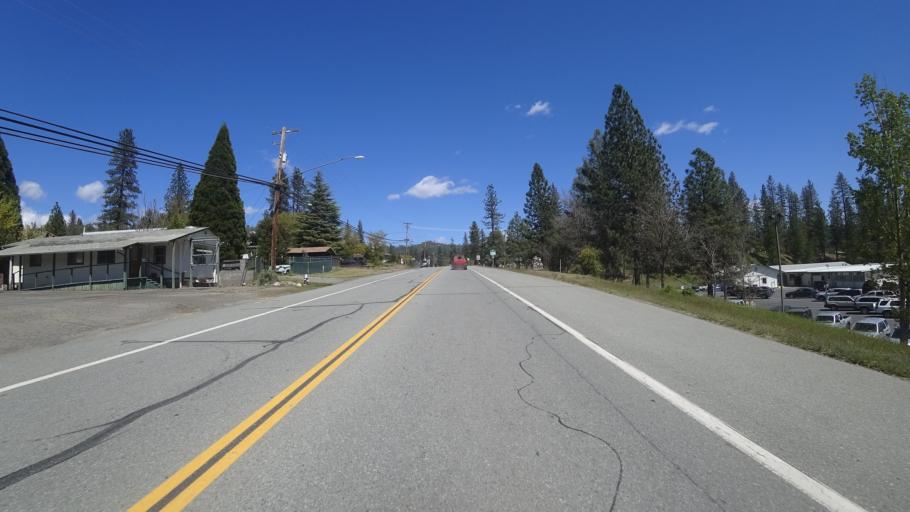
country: US
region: California
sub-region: Trinity County
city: Weaverville
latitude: 40.7337
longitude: -122.9363
